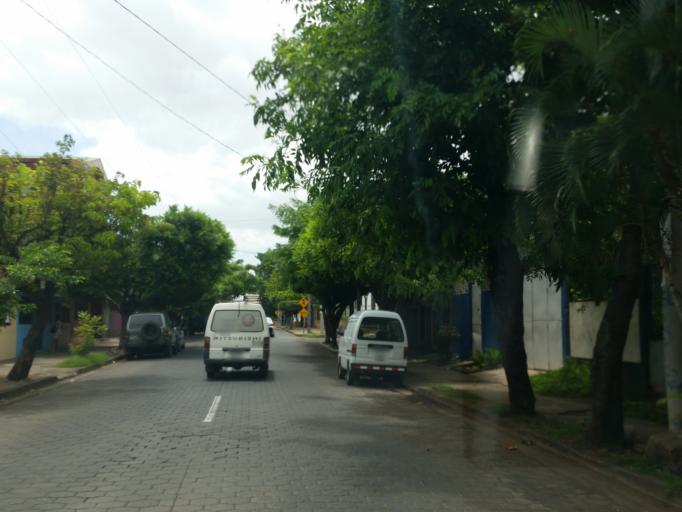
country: NI
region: Managua
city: Managua
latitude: 12.1262
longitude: -86.2532
